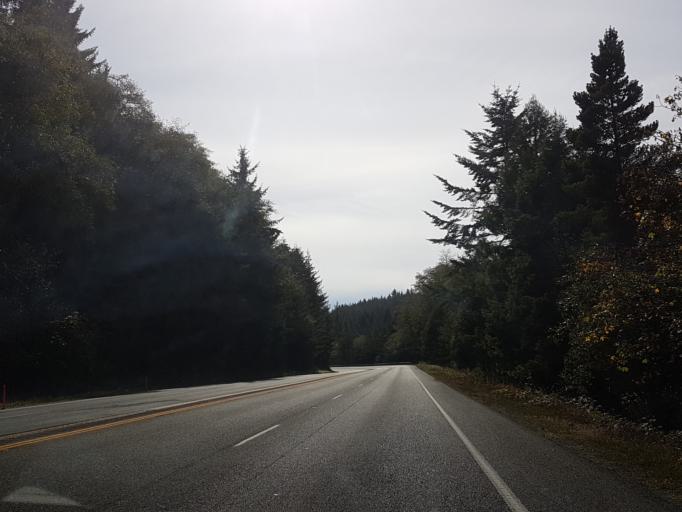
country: US
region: California
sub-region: Del Norte County
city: Bertsch-Oceanview
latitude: 41.4886
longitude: -124.0494
